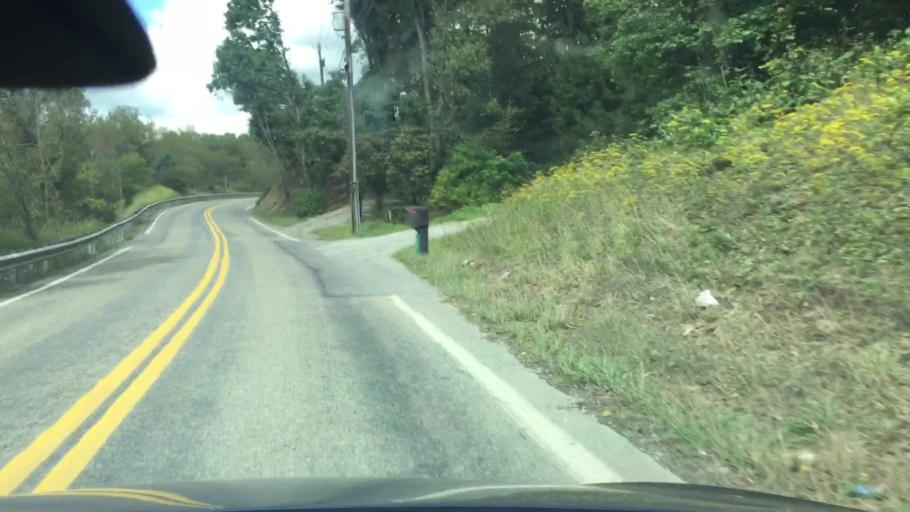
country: US
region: Pennsylvania
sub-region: Allegheny County
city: Curtisville
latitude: 40.6487
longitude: -79.8389
